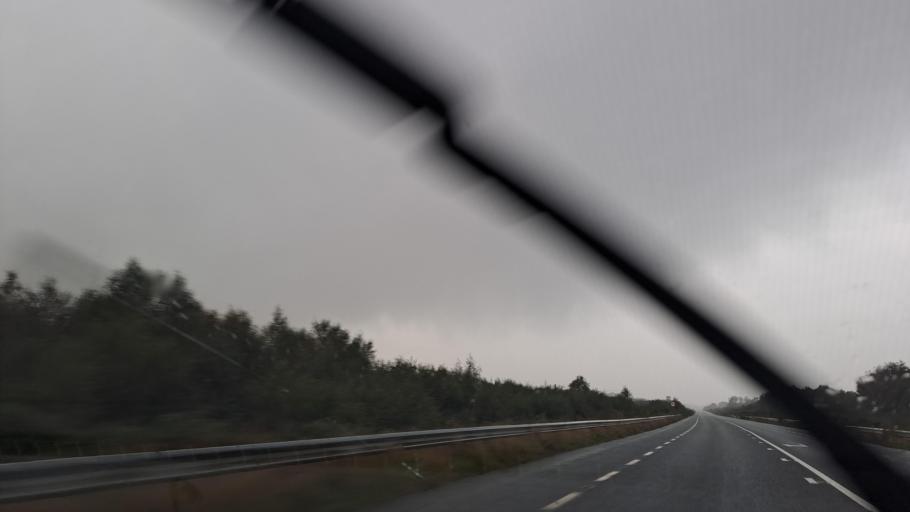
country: IE
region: Ulster
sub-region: County Monaghan
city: Carrickmacross
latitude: 53.9727
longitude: -6.6131
